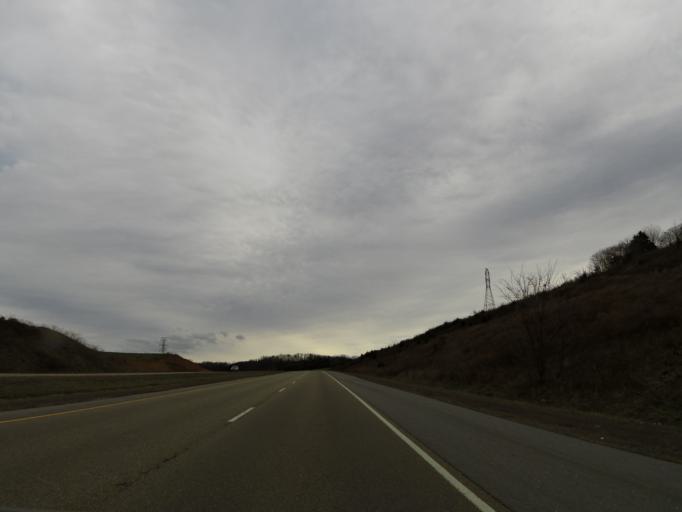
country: US
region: Tennessee
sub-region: Cocke County
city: Newport
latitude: 36.0053
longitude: -83.0774
